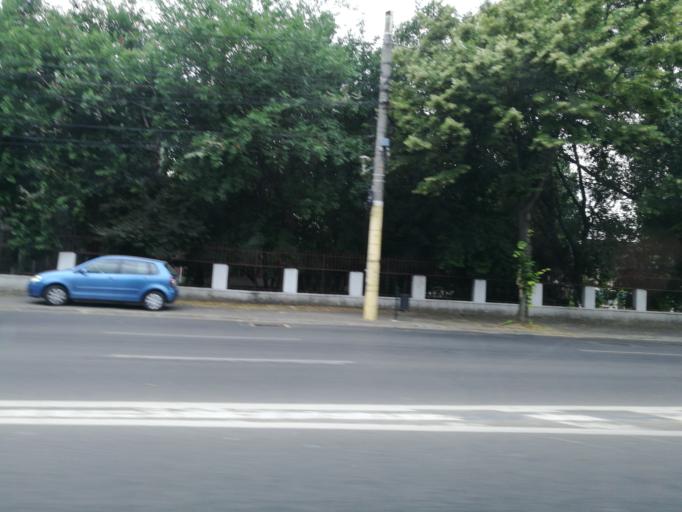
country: RO
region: Constanta
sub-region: Municipiul Constanta
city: Constanta
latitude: 44.1846
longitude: 28.6354
